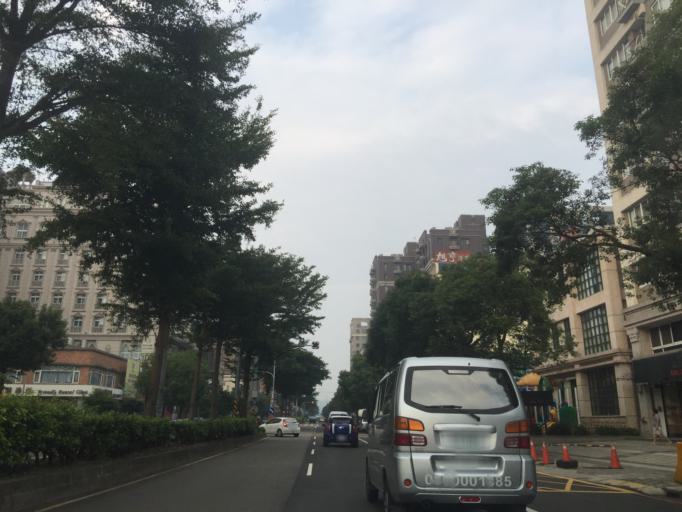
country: TW
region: Taiwan
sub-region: Hsinchu
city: Zhubei
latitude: 24.8301
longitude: 121.0177
